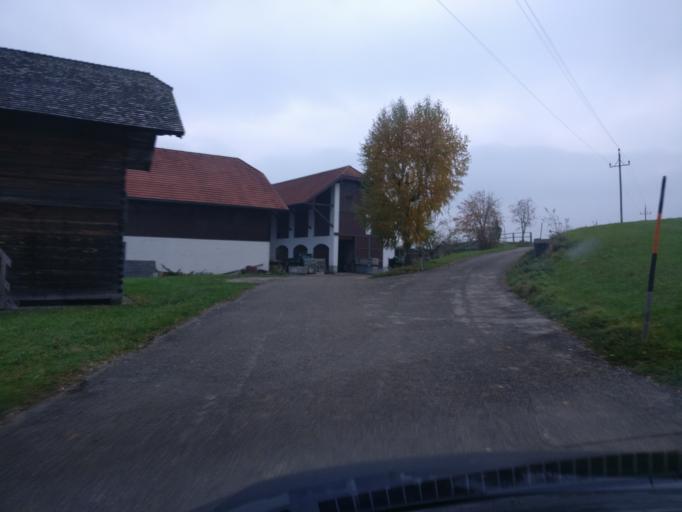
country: AT
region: Salzburg
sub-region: Politischer Bezirk Salzburg-Umgebung
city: Hallwang
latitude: 47.8616
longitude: 13.0786
